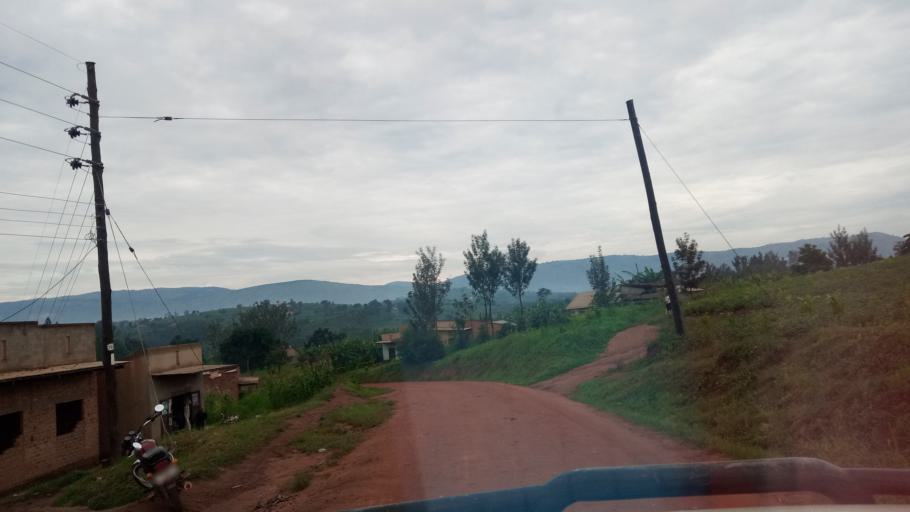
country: UG
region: Western Region
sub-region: Buhweju District
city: Buhweju
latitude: -0.1692
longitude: 30.4642
